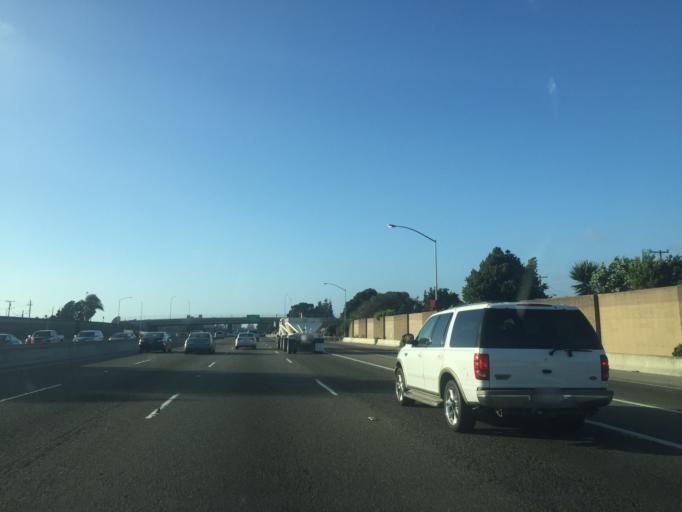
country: US
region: California
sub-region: Alameda County
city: San Leandro
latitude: 37.7171
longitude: -122.1745
